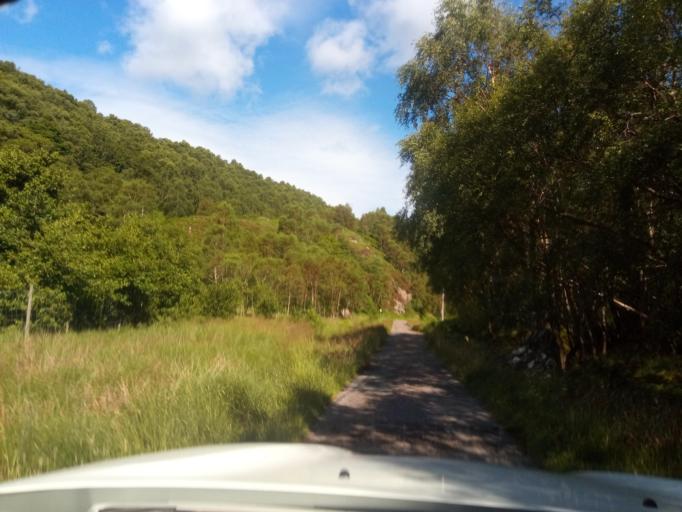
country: GB
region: Scotland
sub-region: Argyll and Bute
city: Isle Of Mull
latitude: 56.7678
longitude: -5.8223
